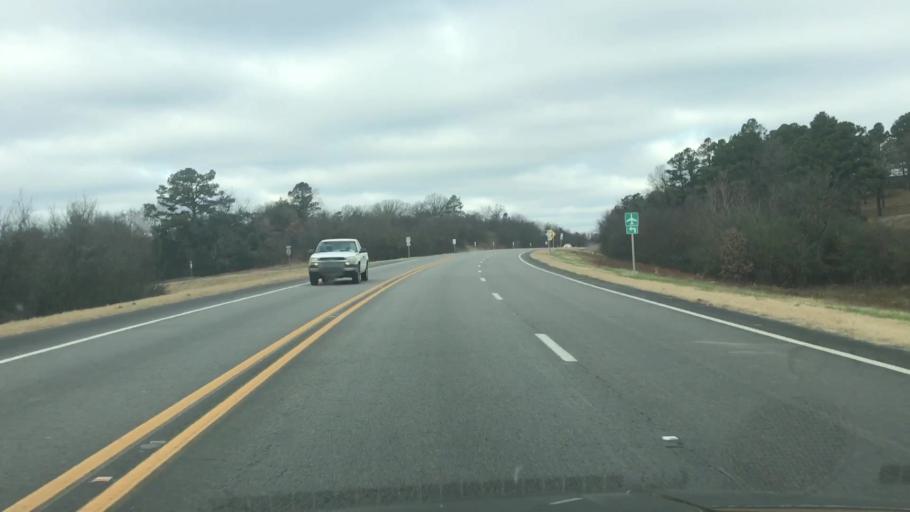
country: US
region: Arkansas
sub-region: Scott County
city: Waldron
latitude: 34.8822
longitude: -94.1040
